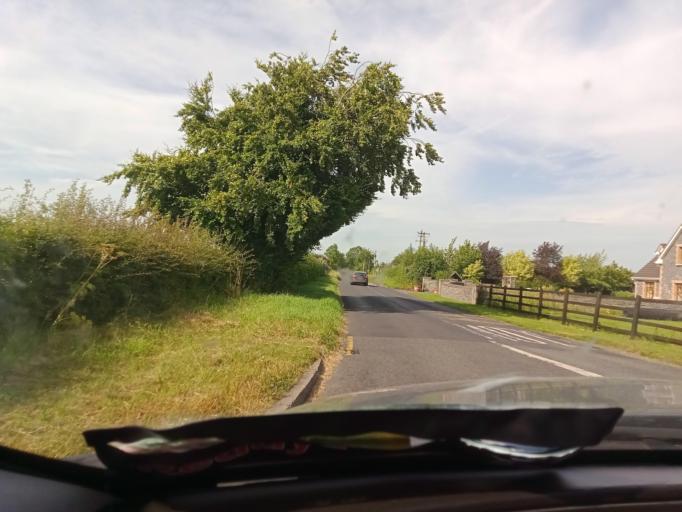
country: IE
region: Leinster
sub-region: Laois
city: Mountmellick
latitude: 53.1246
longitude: -7.3766
